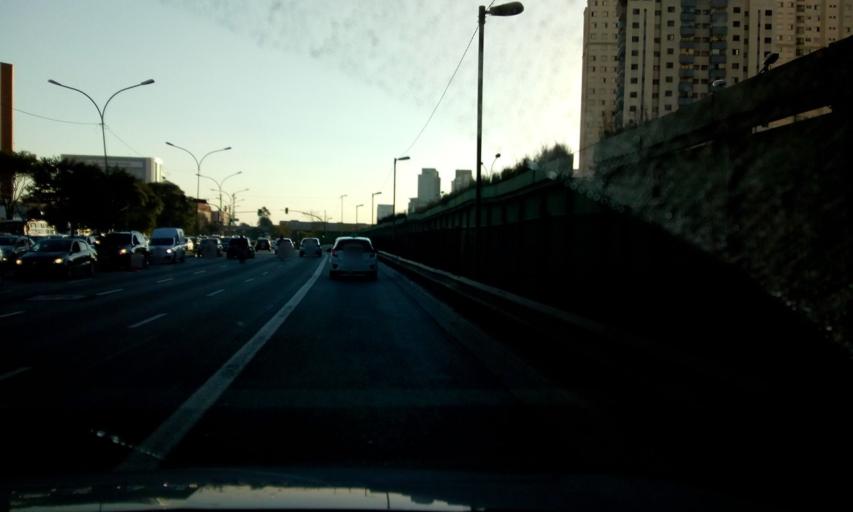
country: BR
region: Sao Paulo
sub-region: Sao Paulo
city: Sao Paulo
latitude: -23.5394
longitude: -46.5716
